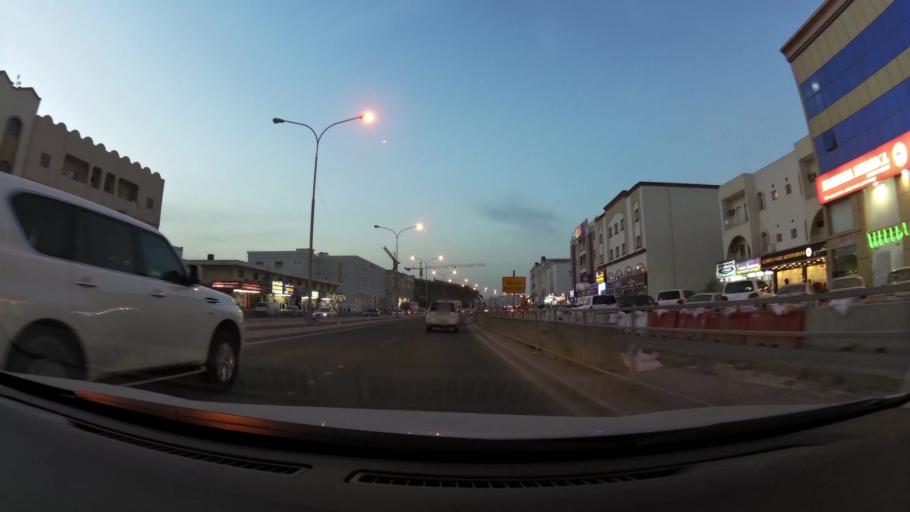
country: QA
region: Al Wakrah
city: Al Wakrah
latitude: 25.1625
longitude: 51.5981
